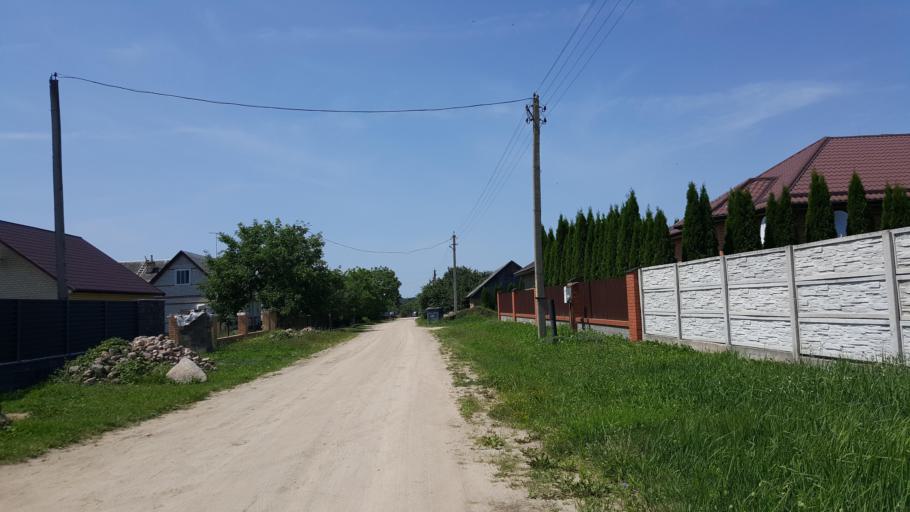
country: BY
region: Brest
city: Vysokaye
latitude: 52.3613
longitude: 23.3927
